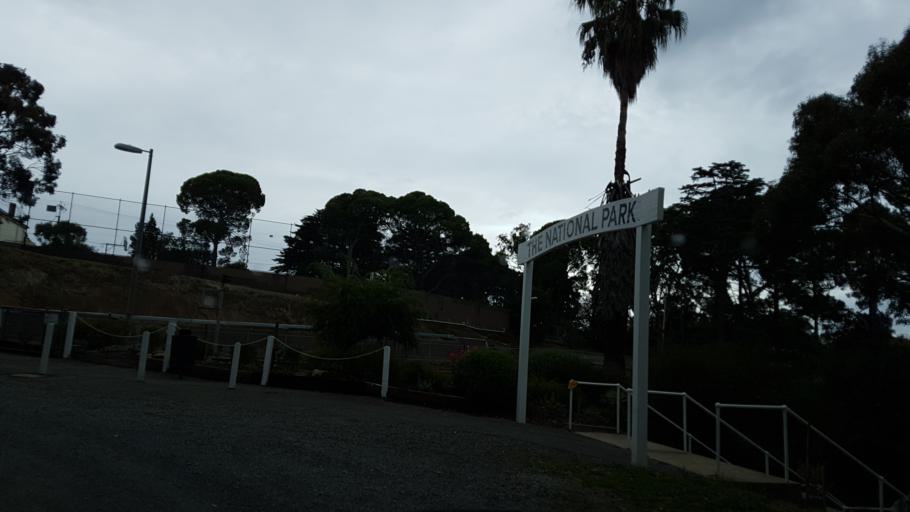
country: AU
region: South Australia
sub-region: Mitcham
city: Belair
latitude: -34.9981
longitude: 138.6338
